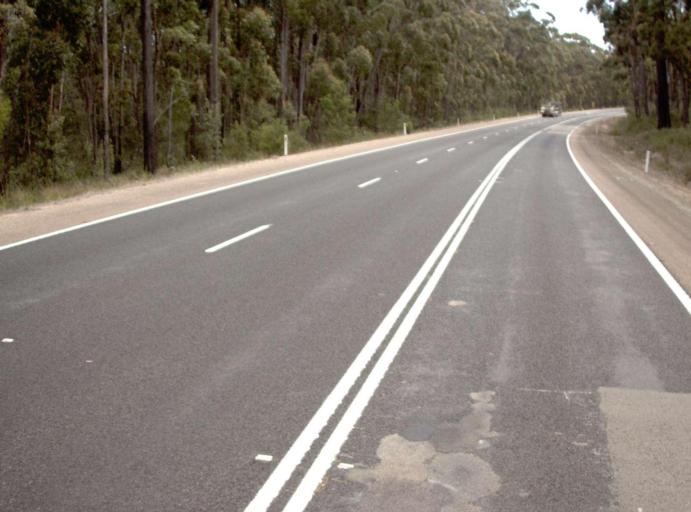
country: AU
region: New South Wales
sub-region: Bega Valley
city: Eden
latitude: -37.5056
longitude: 149.5319
